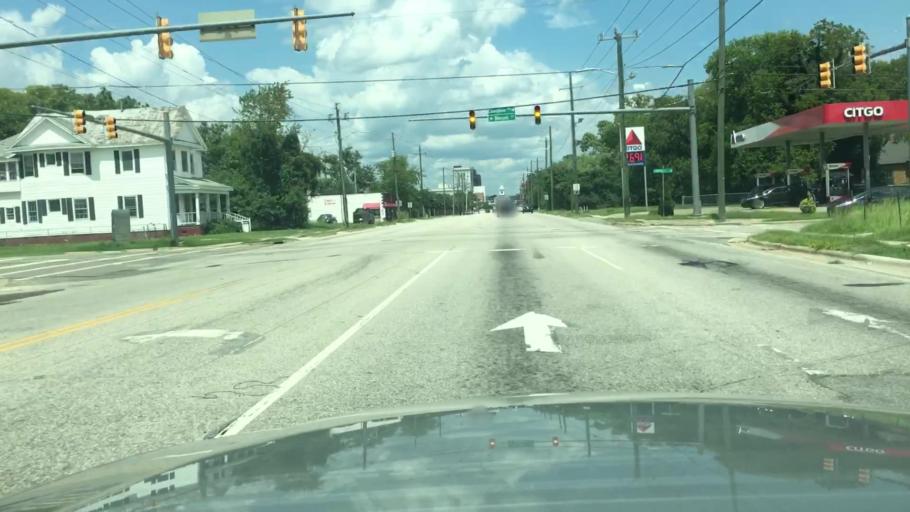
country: US
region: North Carolina
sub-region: Cumberland County
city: Fayetteville
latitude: 35.0460
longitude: -78.8805
